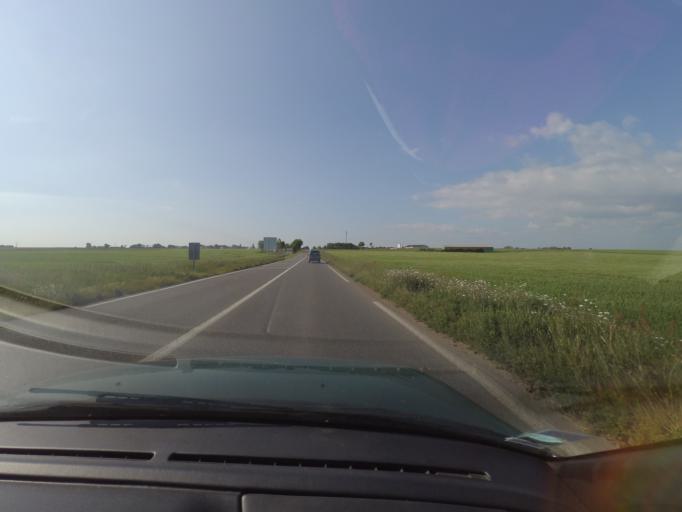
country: FR
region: Pays de la Loire
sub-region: Departement de la Vendee
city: Angles
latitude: 46.4172
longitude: -1.3897
